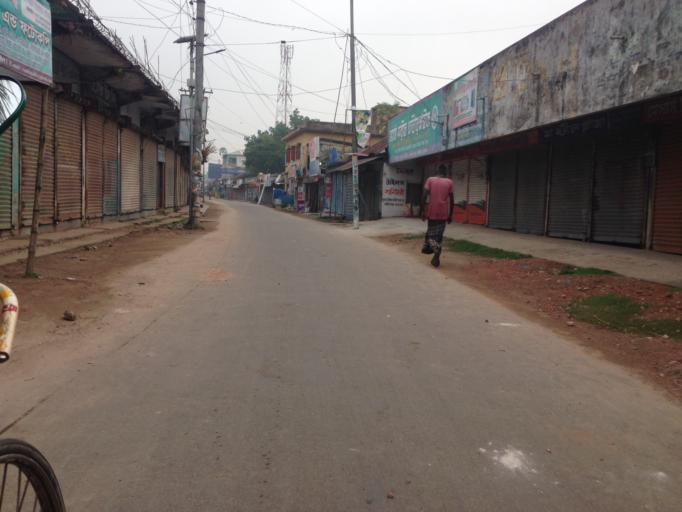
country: BD
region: Khulna
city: Kalia
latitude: 23.0394
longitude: 89.6322
